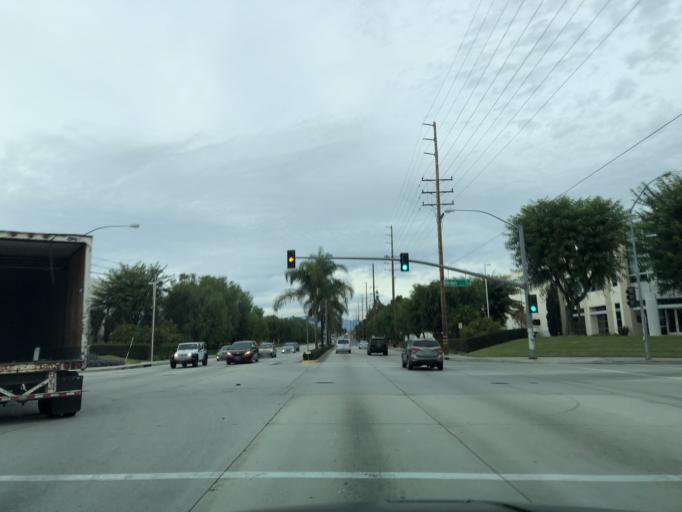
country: US
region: California
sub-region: Los Angeles County
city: La Mirada
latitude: 33.9114
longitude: -118.0467
